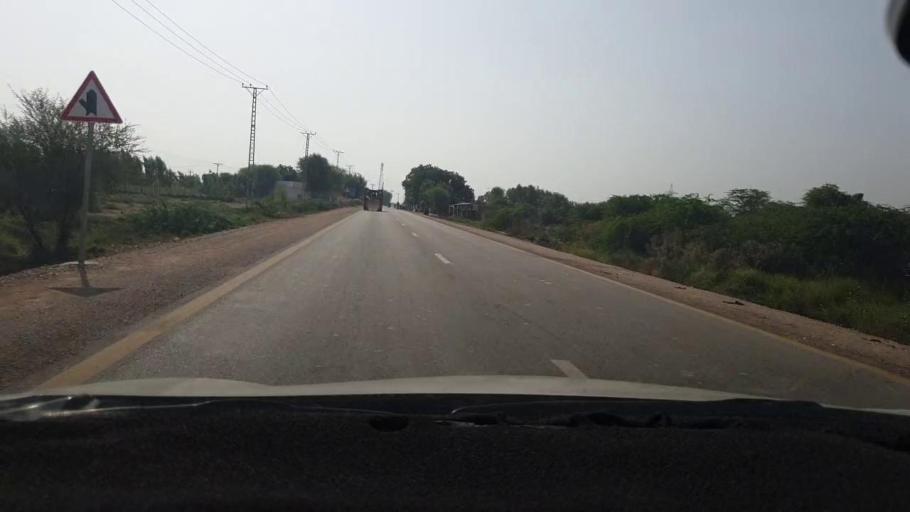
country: PK
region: Sindh
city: Jhol
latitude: 25.9438
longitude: 68.9849
